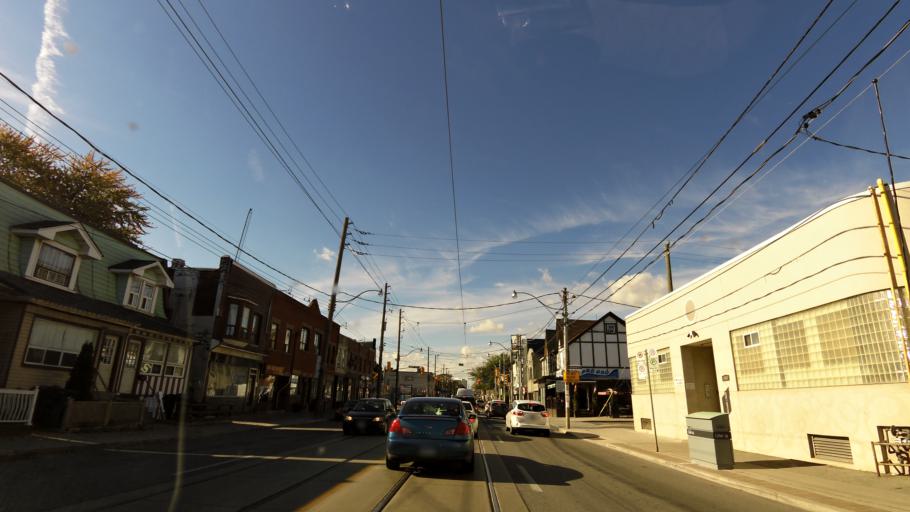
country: CA
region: Ontario
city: Toronto
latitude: 43.6517
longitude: -79.4472
